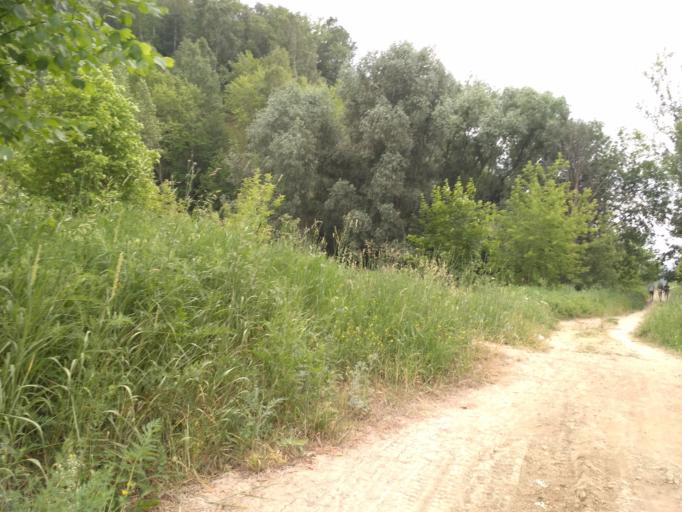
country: RU
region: Nizjnij Novgorod
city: Nizhniy Novgorod
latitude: 56.2768
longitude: 43.9712
